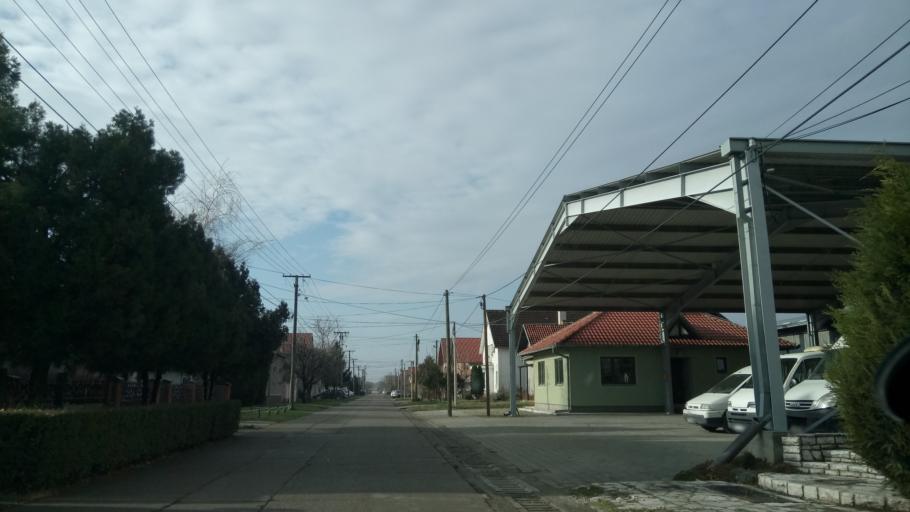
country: RS
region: Autonomna Pokrajina Vojvodina
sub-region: Sremski Okrug
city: Stara Pazova
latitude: 44.9772
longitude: 20.1556
